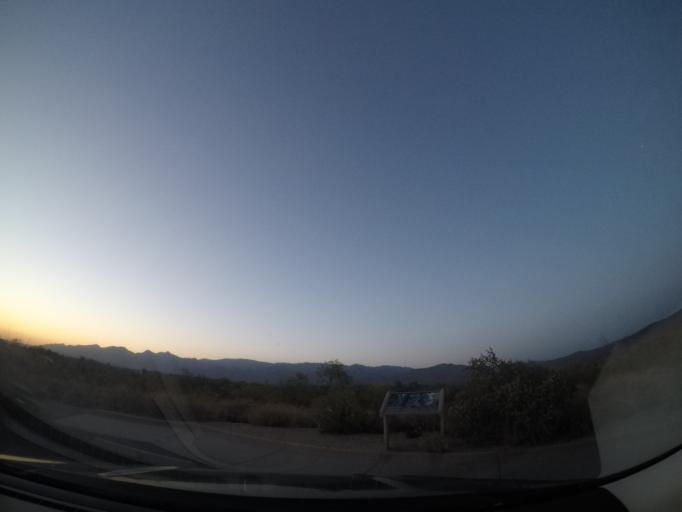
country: US
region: Arizona
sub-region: Pima County
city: Tanque Verde
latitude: 32.1794
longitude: -110.7347
